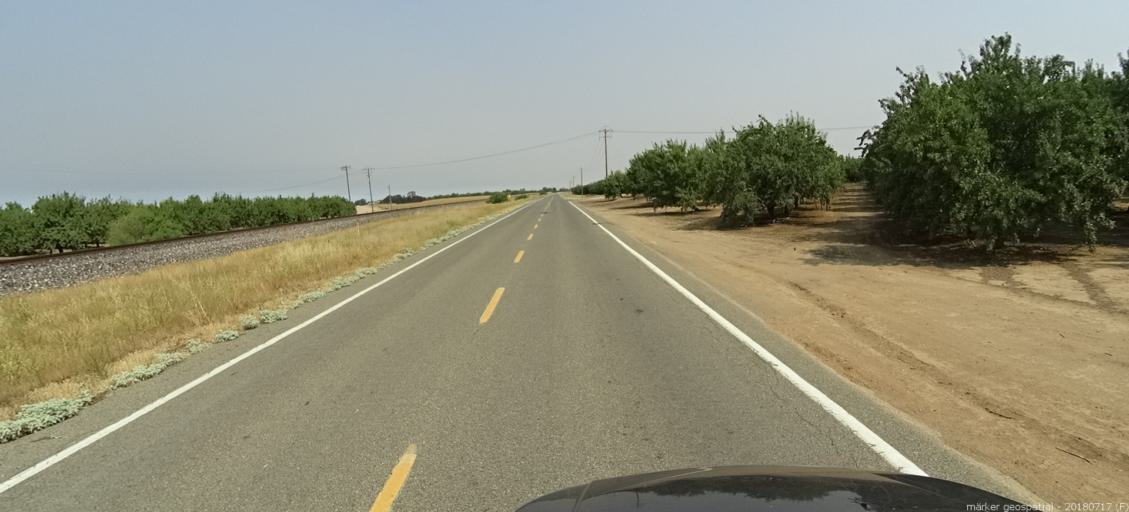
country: US
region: California
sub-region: Madera County
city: Fairmead
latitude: 37.1333
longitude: -120.1555
